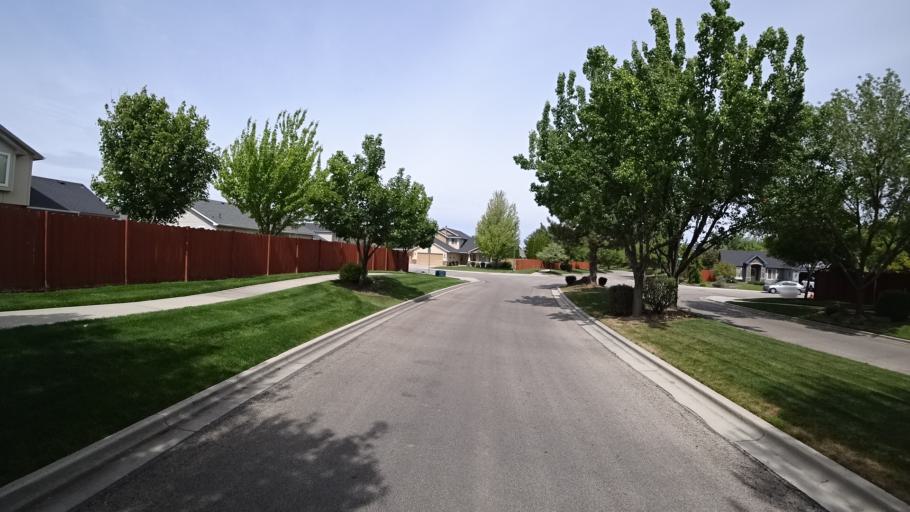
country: US
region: Idaho
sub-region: Ada County
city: Meridian
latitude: 43.5518
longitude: -116.3356
